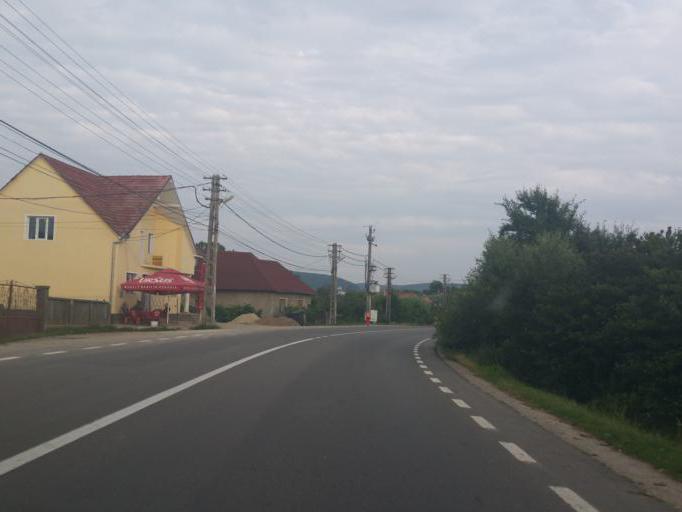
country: RO
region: Salaj
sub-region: Comuna Hida
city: Hida
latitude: 47.0425
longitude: 23.2577
